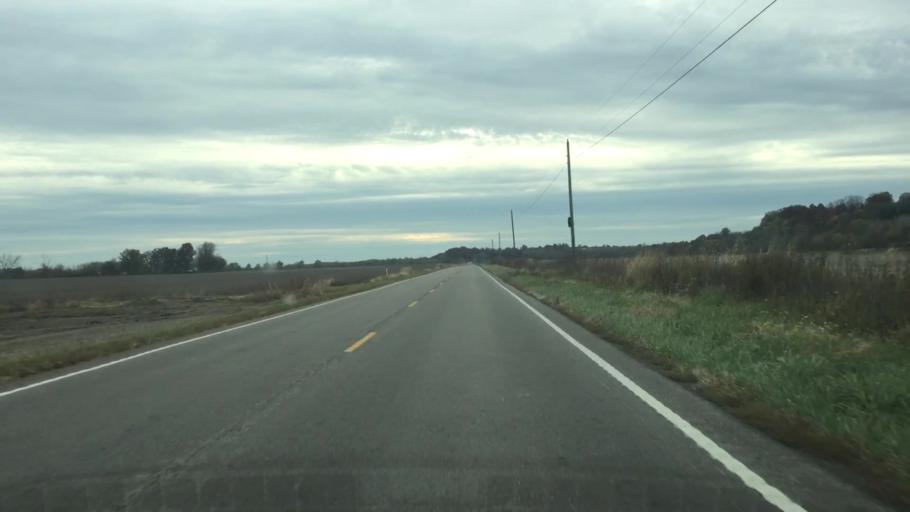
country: US
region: Missouri
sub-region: Callaway County
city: Fulton
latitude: 38.7051
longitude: -91.8007
